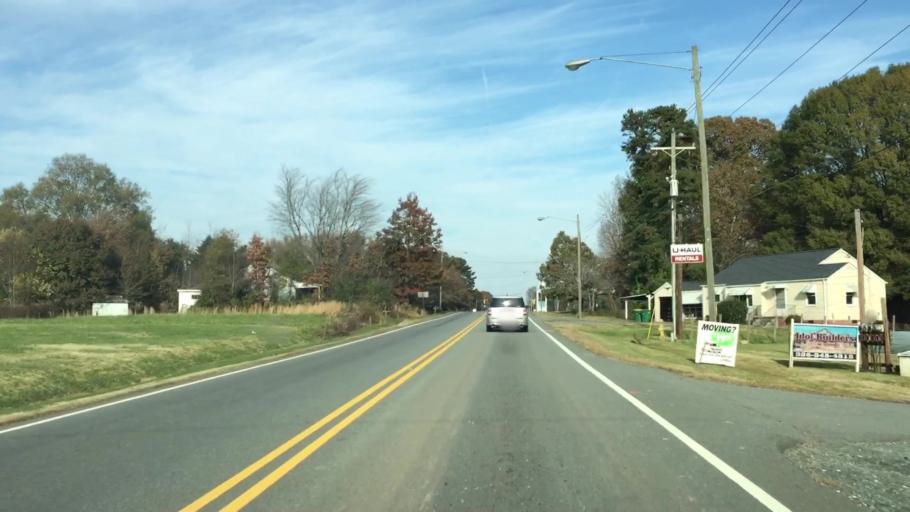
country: US
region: North Carolina
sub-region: Forsyth County
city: Walkertown
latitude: 36.1541
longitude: -80.1483
